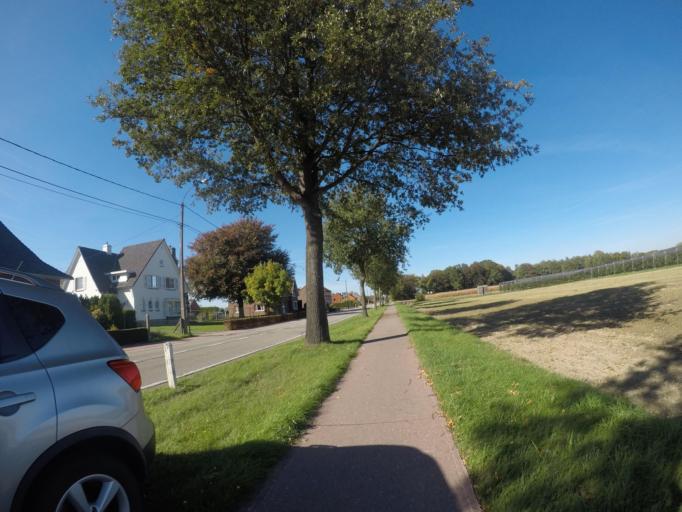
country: BE
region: Flanders
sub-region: Provincie Limburg
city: Alken
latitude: 50.8899
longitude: 5.2886
